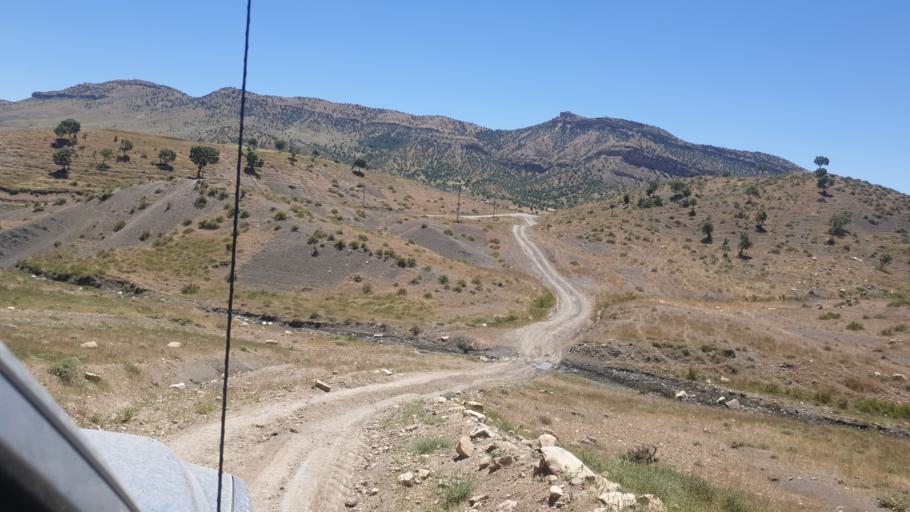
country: IQ
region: Arbil
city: Nahiyat Hiran
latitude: 36.2019
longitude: 44.4231
